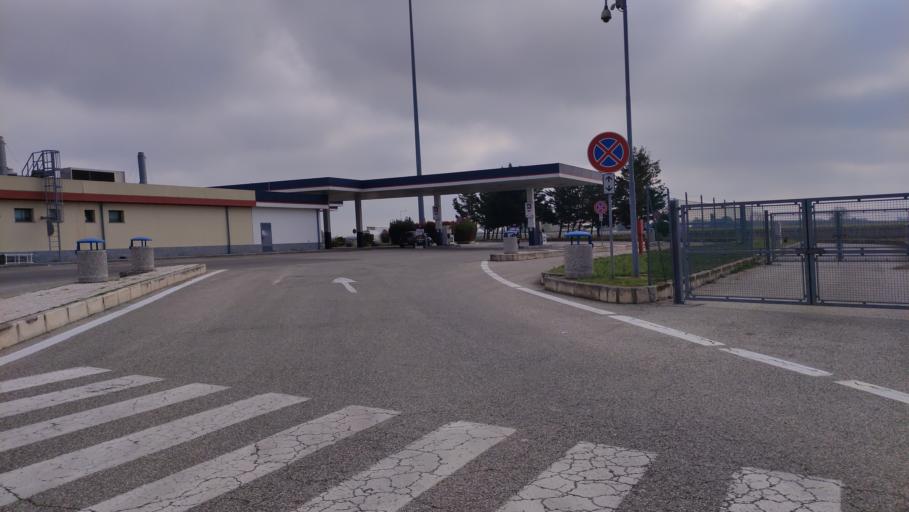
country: IT
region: Emilia-Romagna
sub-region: Provincia di Ravenna
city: Russi
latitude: 44.4015
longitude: 12.0461
